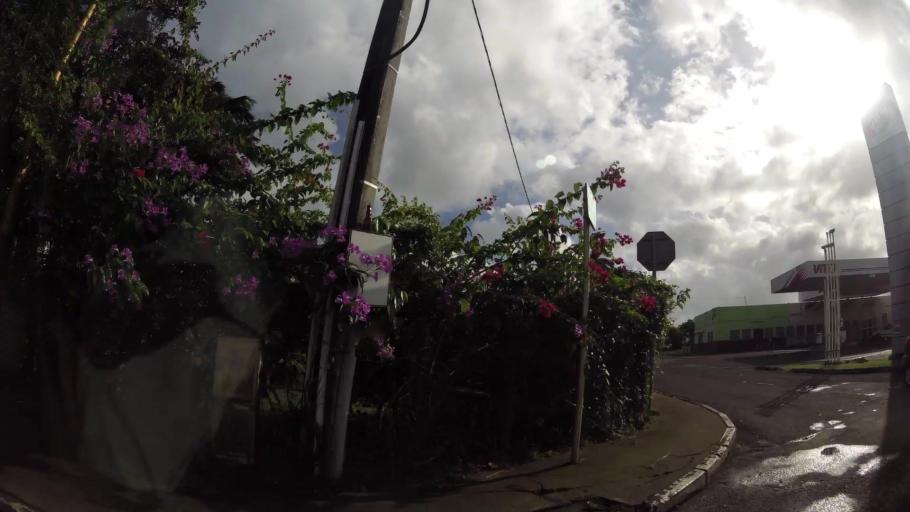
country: MQ
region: Martinique
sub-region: Martinique
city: Ducos
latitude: 14.5458
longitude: -60.9708
